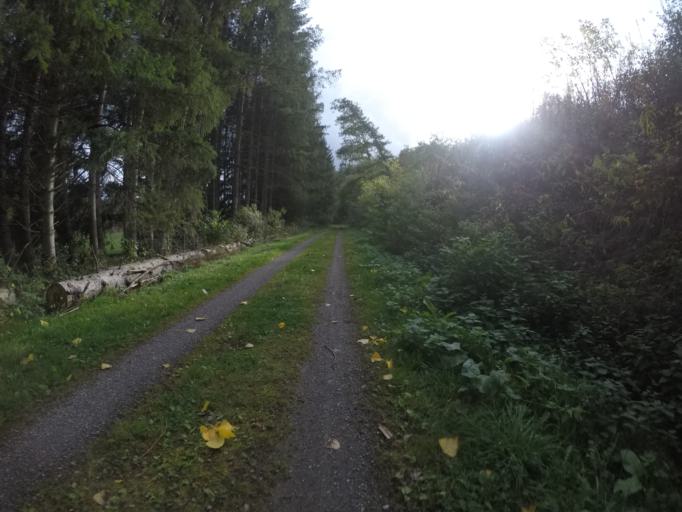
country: BE
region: Wallonia
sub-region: Province du Luxembourg
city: Fauvillers
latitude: 49.8897
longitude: 5.6756
